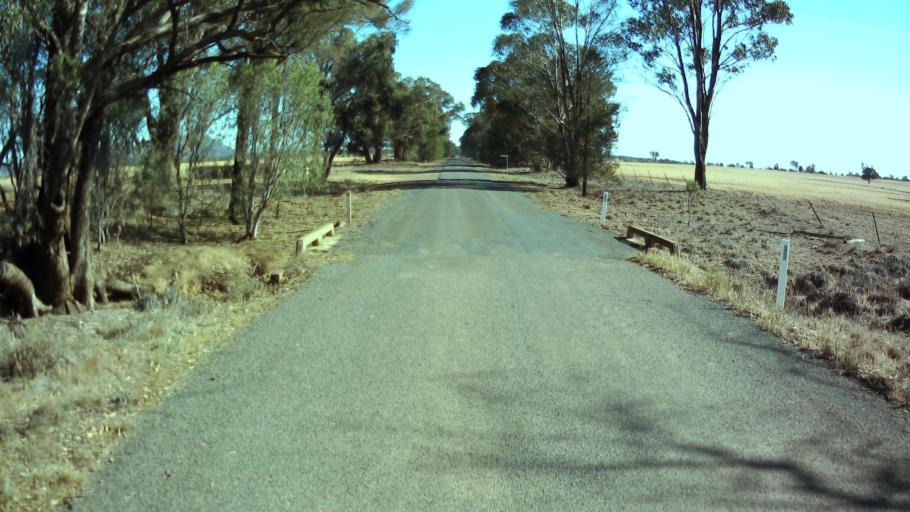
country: AU
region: New South Wales
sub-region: Weddin
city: Grenfell
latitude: -33.8064
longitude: 147.9548
